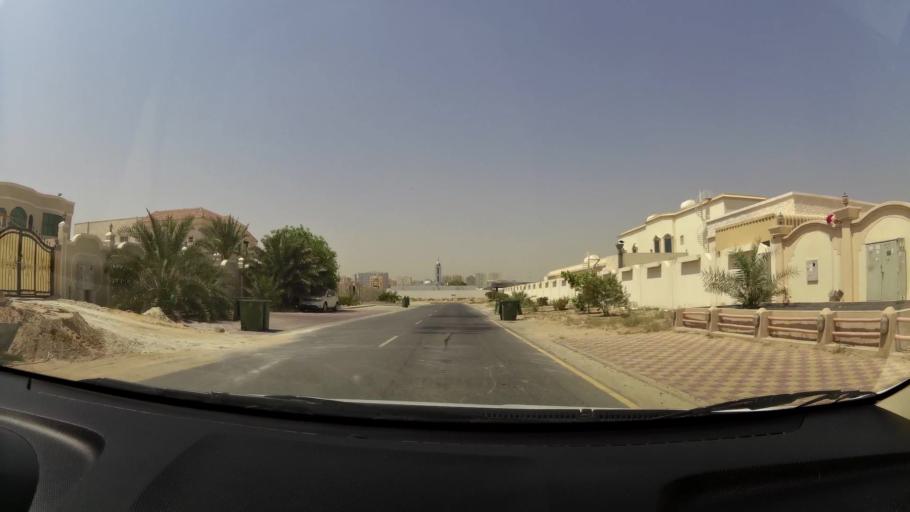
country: AE
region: Ajman
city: Ajman
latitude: 25.4157
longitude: 55.5138
